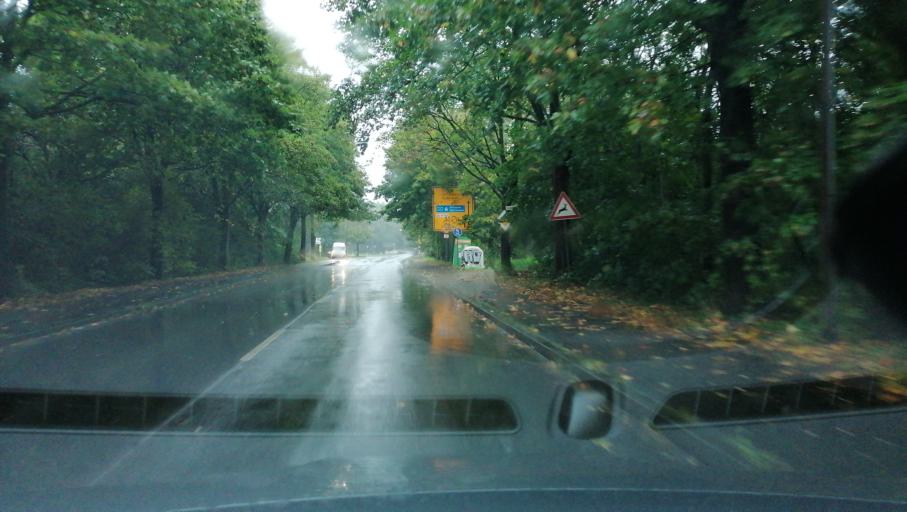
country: DE
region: North Rhine-Westphalia
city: Oer-Erkenschwick
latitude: 51.5889
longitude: 7.2563
